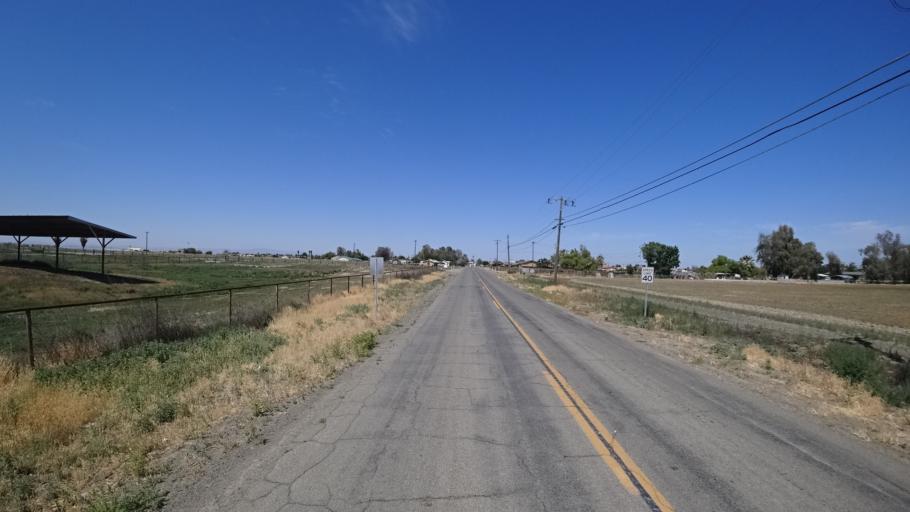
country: US
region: California
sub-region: Kings County
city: Stratford
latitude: 36.1894
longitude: -119.8153
